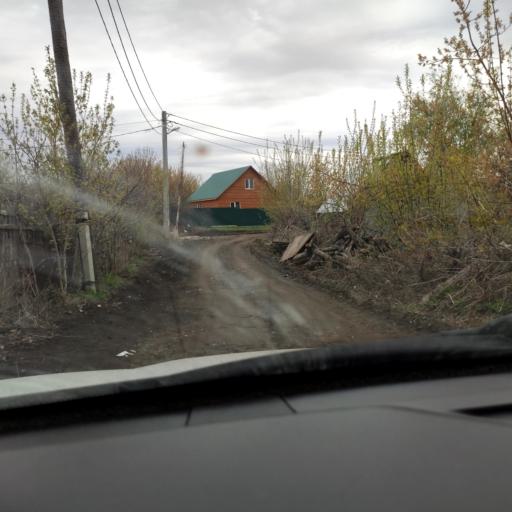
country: RU
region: Samara
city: Petra-Dubrava
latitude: 53.2598
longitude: 50.3438
